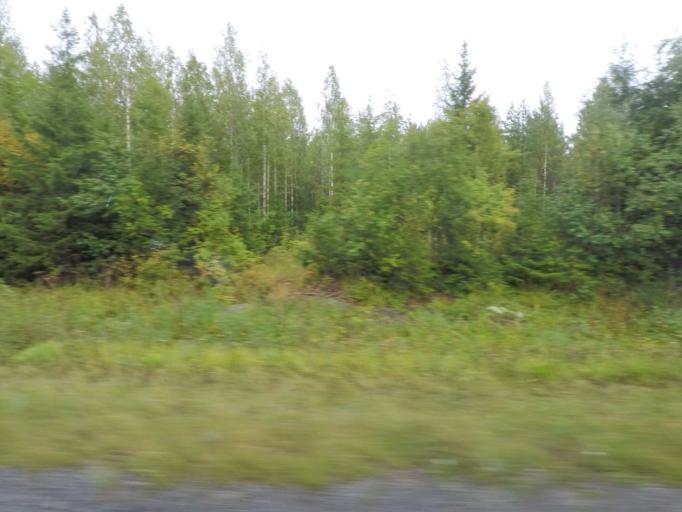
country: FI
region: Southern Savonia
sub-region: Pieksaemaeki
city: Juva
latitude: 62.0163
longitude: 27.7996
